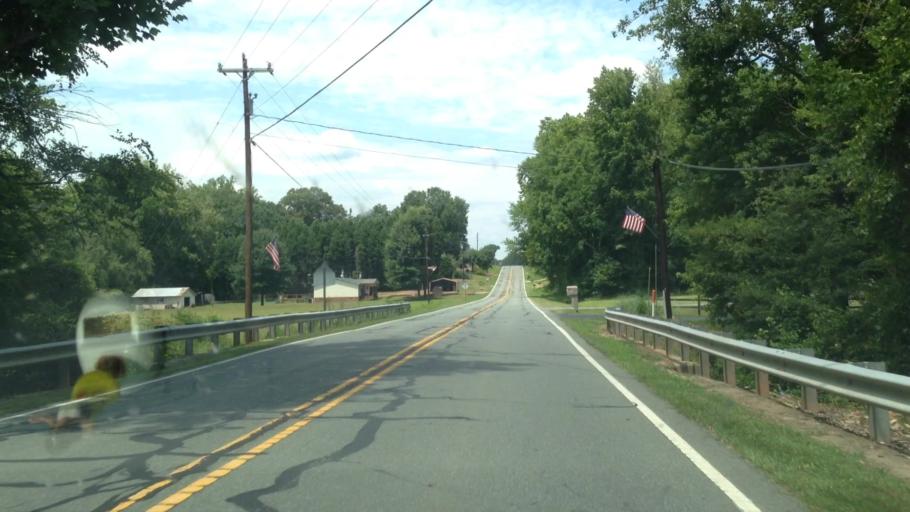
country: US
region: North Carolina
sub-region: Stokes County
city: Walnut Cove
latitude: 36.3328
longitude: -80.0485
